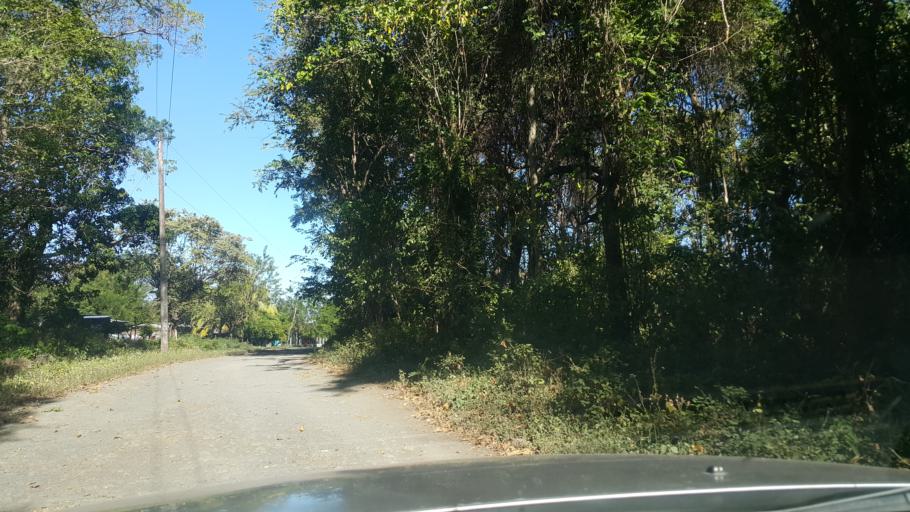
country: NI
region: Rivas
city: Altagracia
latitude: 11.4903
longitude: -85.6049
